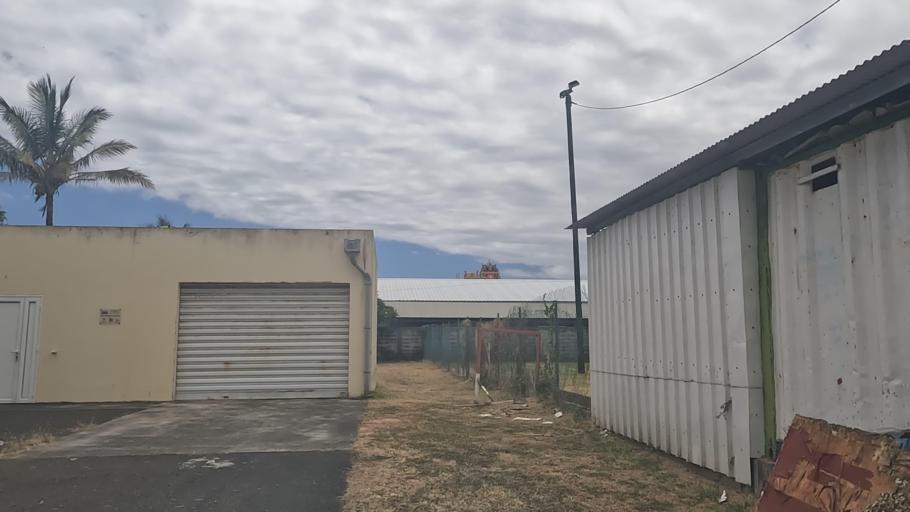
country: RE
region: Reunion
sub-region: Reunion
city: Saint-Benoit
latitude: -21.0343
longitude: 55.7180
